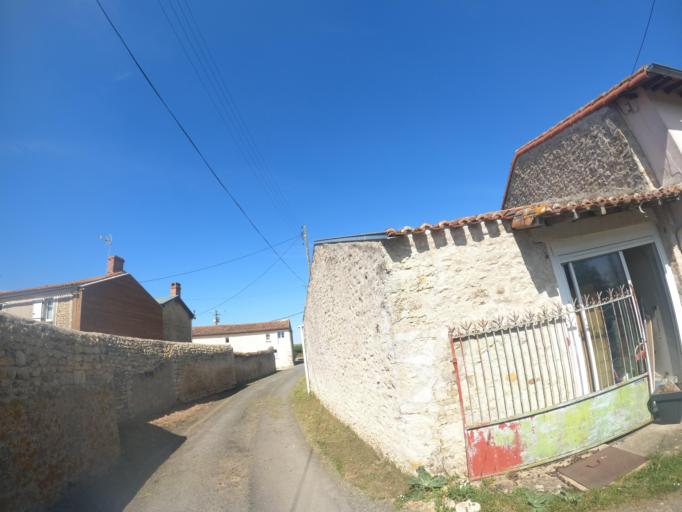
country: FR
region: Poitou-Charentes
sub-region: Departement des Deux-Sevres
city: Airvault
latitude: 46.8789
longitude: -0.1668
